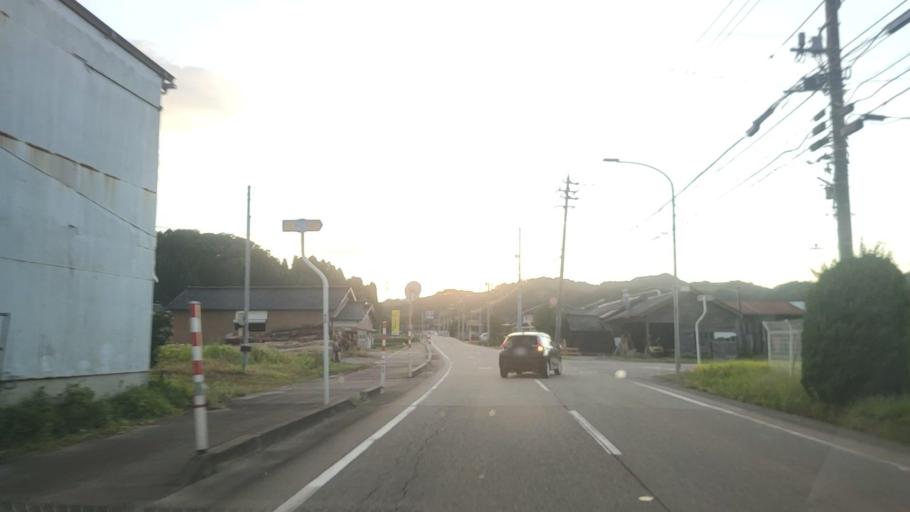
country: JP
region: Toyama
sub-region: Oyabe Shi
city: Oyabe
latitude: 36.6322
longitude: 136.8308
